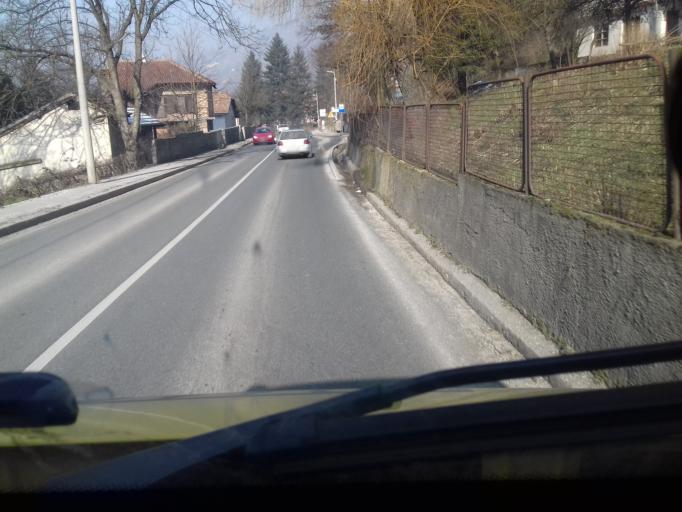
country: BA
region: Federation of Bosnia and Herzegovina
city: Ilijas
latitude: 43.9299
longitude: 18.3037
